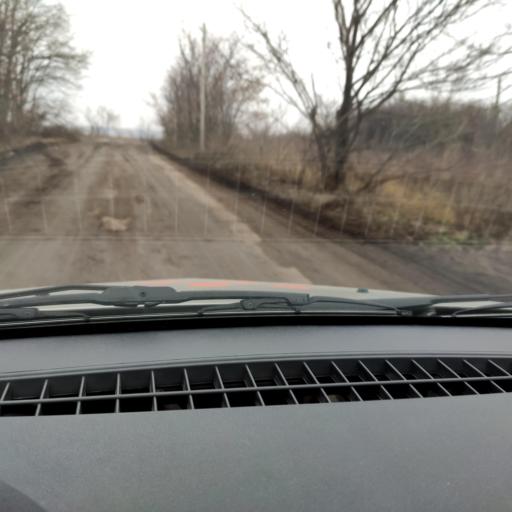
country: RU
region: Bashkortostan
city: Ufa
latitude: 54.5787
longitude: 55.8840
